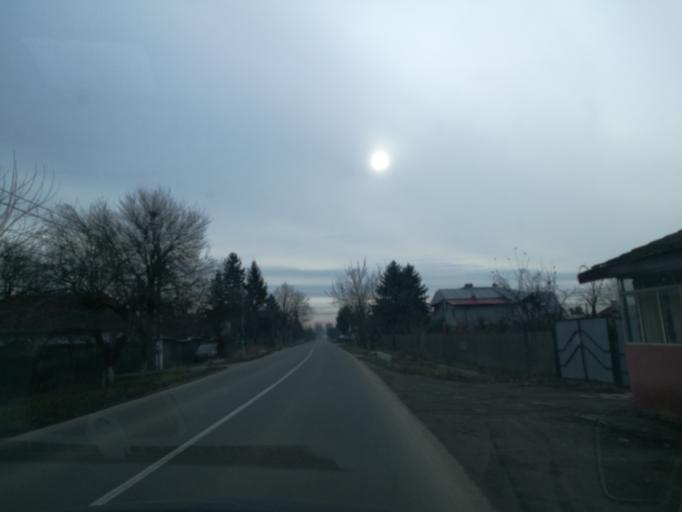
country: RO
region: Ilfov
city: Dascalu
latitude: 44.5999
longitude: 26.2411
